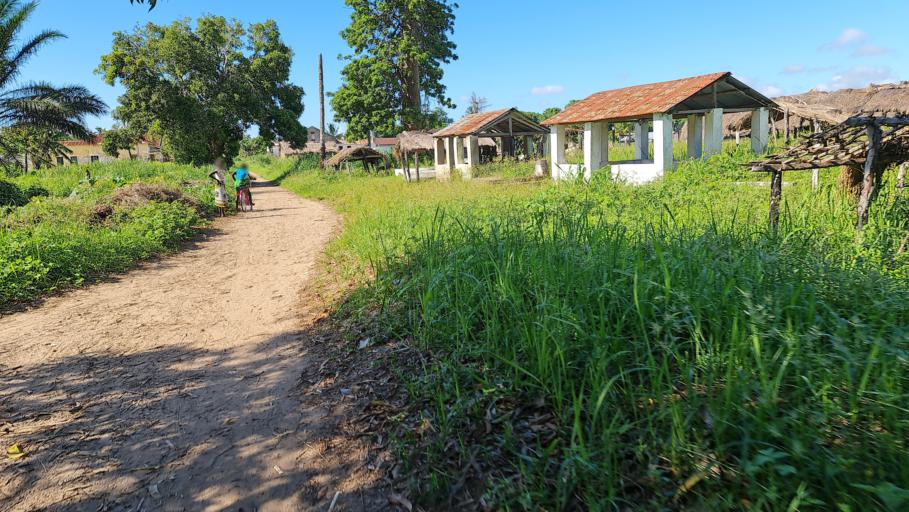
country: MZ
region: Zambezia
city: Quelimane
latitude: -17.4428
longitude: 37.6988
